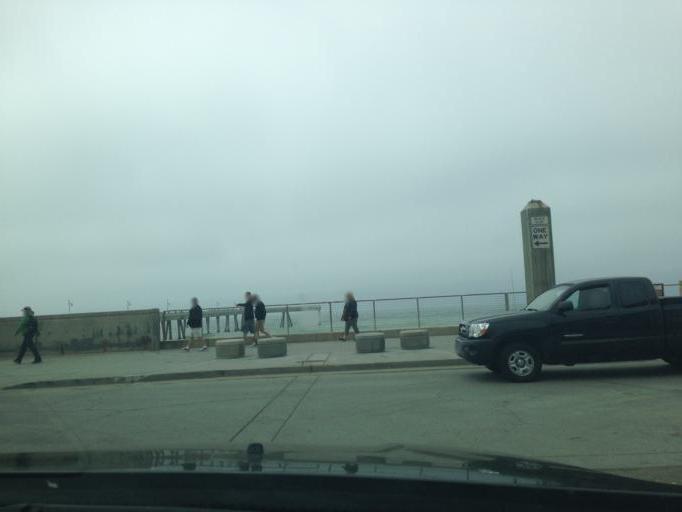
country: US
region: California
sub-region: San Mateo County
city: Pacifica
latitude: 37.6340
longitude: -122.4940
